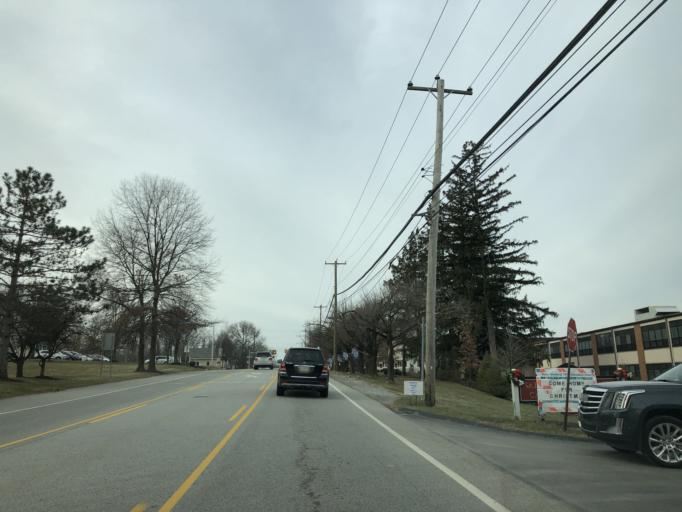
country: US
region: Pennsylvania
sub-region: Chester County
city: Exton
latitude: 40.0300
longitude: -75.6075
